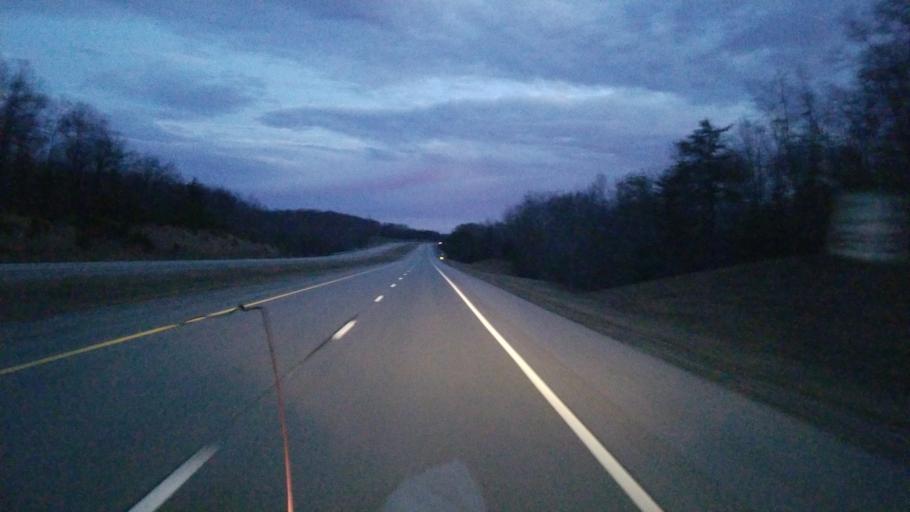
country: US
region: Tennessee
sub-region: Van Buren County
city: Spencer
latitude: 35.5742
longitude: -85.4716
